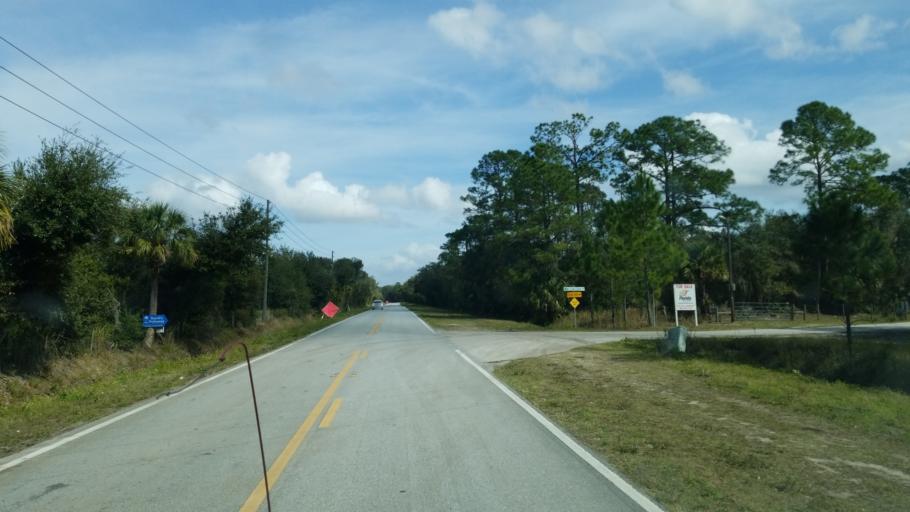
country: US
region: Florida
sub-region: Polk County
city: Babson Park
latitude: 27.9369
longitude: -81.4330
